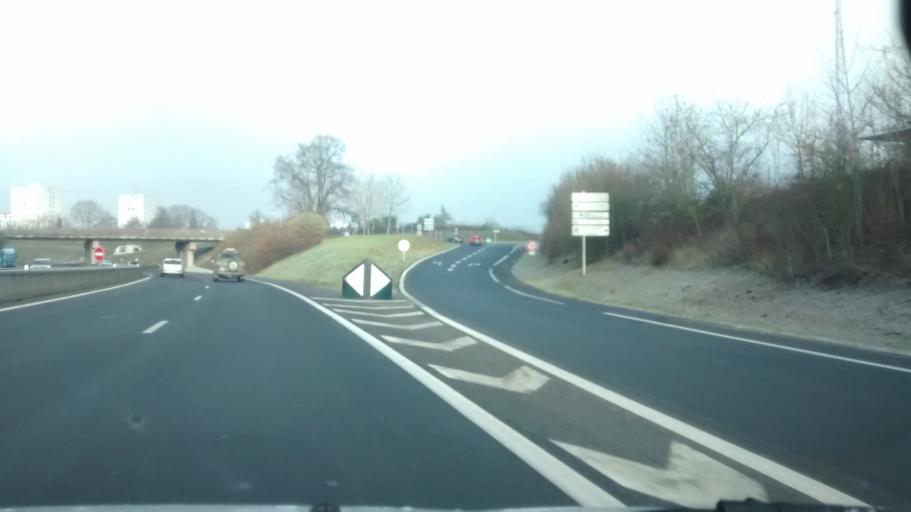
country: FR
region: Centre
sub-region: Departement d'Indre-et-Loire
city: Joue-les-Tours
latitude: 47.3386
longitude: 0.6683
